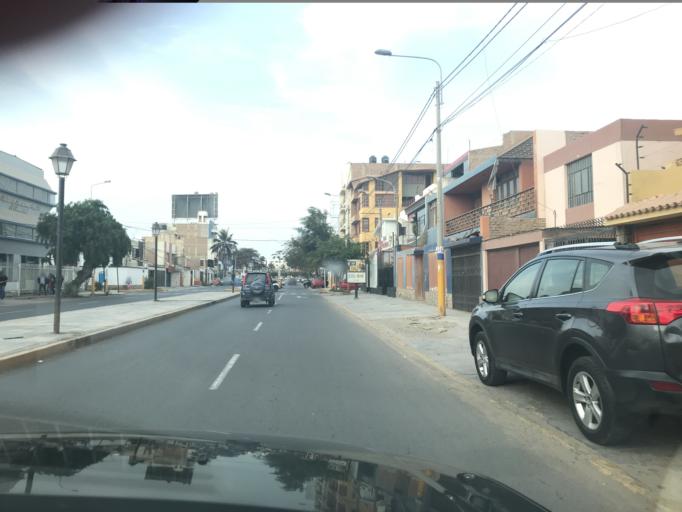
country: PE
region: Lambayeque
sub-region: Provincia de Chiclayo
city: Chiclayo
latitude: -6.7842
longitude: -79.8434
